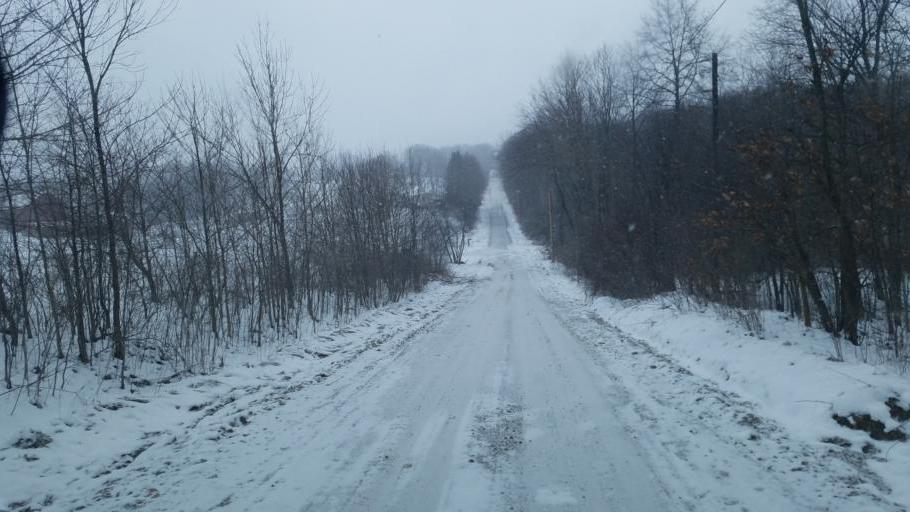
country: US
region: Pennsylvania
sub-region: Mercer County
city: Stoneboro
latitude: 41.3993
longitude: -80.0078
